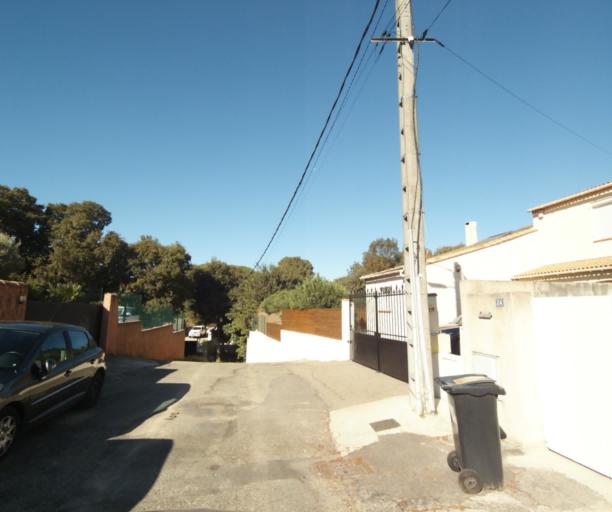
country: FR
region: Languedoc-Roussillon
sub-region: Departement du Gard
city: Bouillargues
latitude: 43.7984
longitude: 4.4190
